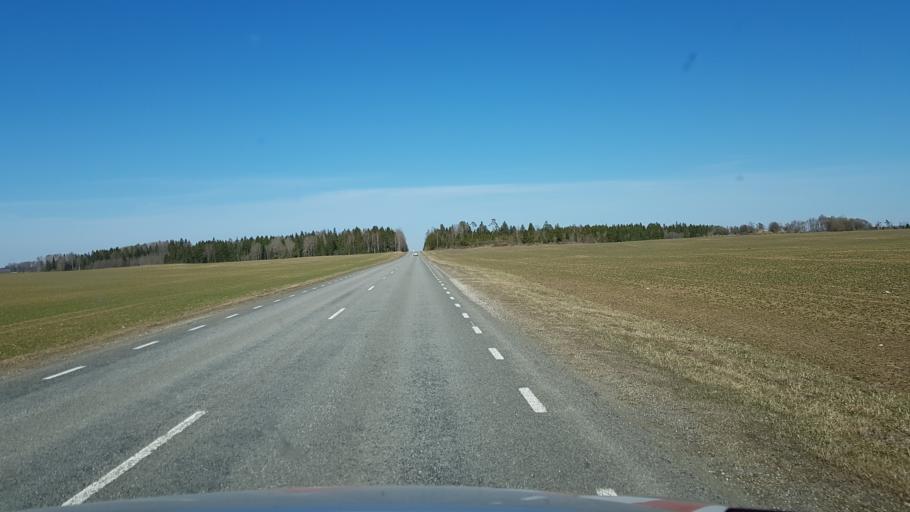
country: EE
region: Laeaene-Virumaa
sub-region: Tamsalu vald
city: Tamsalu
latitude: 59.1201
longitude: 26.0266
